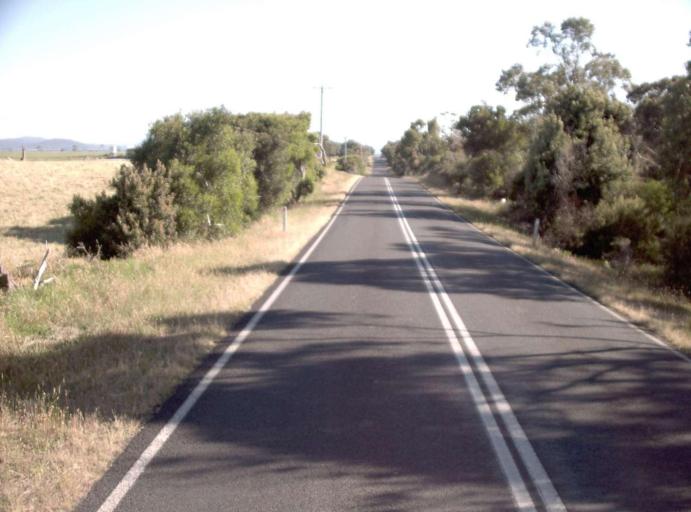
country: AU
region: Victoria
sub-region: Latrobe
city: Morwell
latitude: -38.7032
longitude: 146.3982
